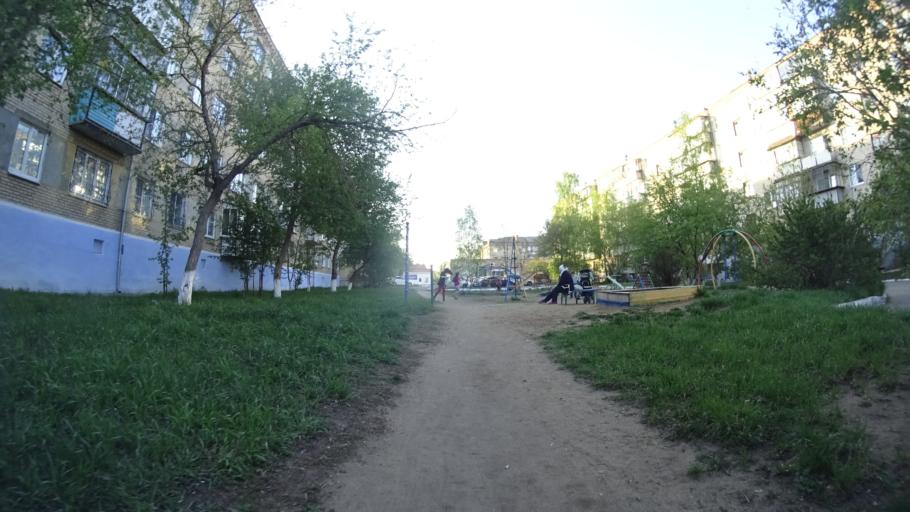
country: RU
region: Chelyabinsk
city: Troitsk
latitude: 54.0813
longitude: 61.5380
